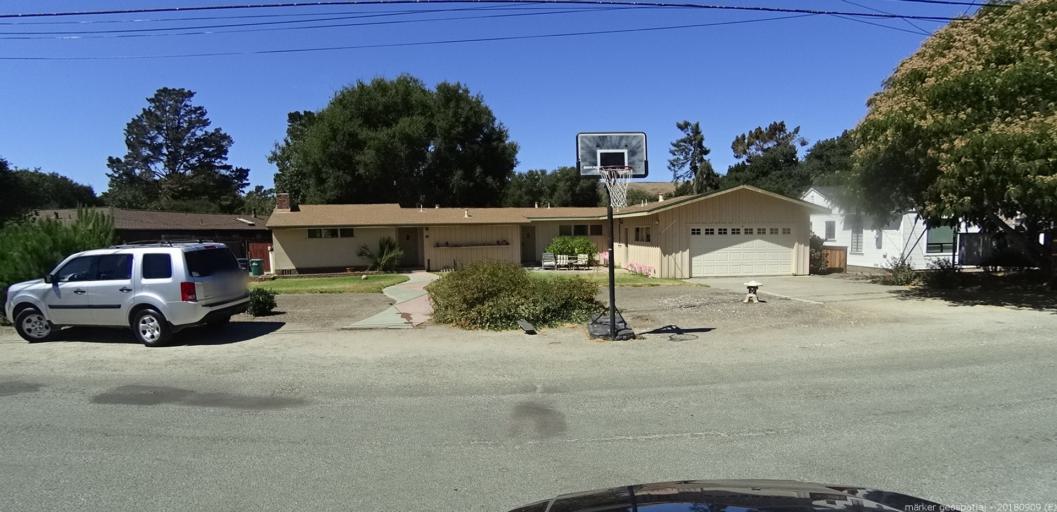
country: US
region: California
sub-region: Monterey County
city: Carmel Valley Village
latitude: 36.5760
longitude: -121.7214
